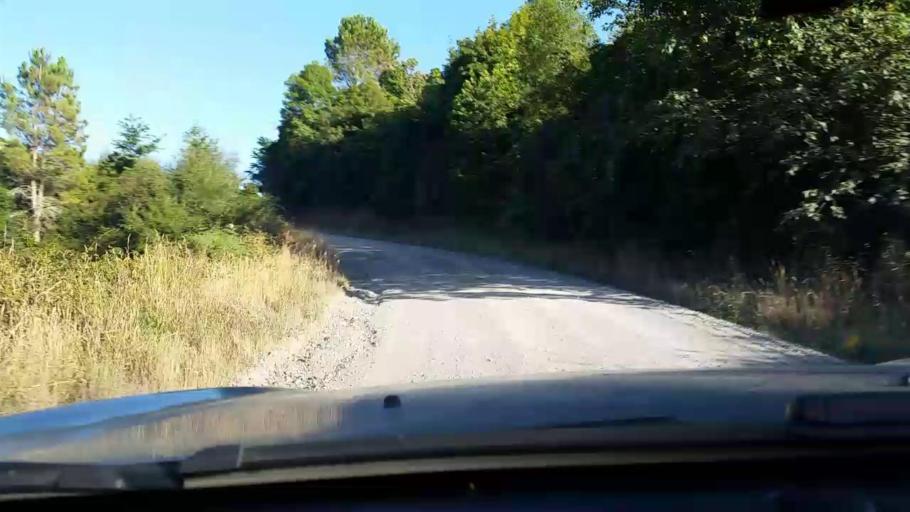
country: NZ
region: Waikato
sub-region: Taupo District
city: Taupo
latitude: -38.4913
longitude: 176.1922
